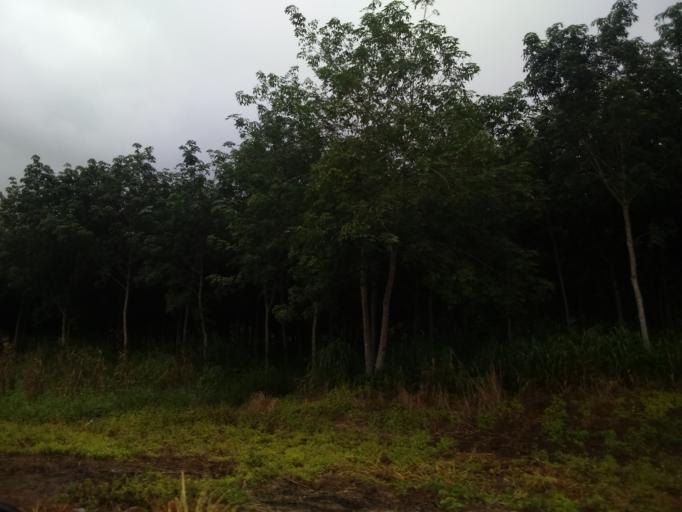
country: CI
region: Sud-Comoe
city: Adiake
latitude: 5.2999
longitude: -3.3460
